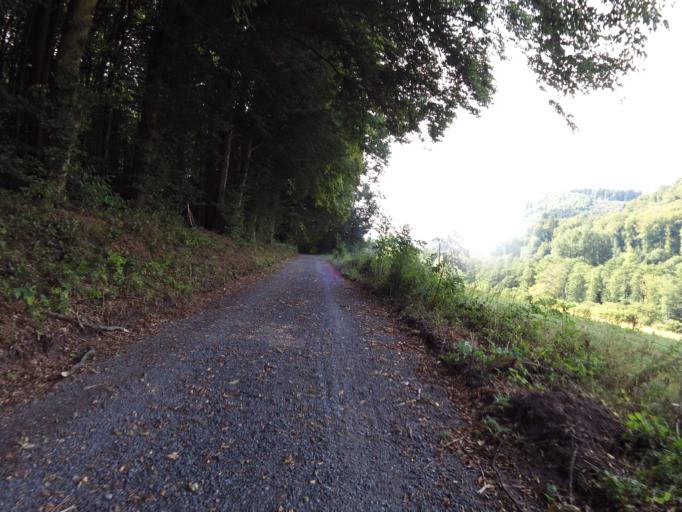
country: DE
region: Baden-Wuerttemberg
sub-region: Karlsruhe Region
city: Neckargemund
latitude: 49.3768
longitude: 8.7897
